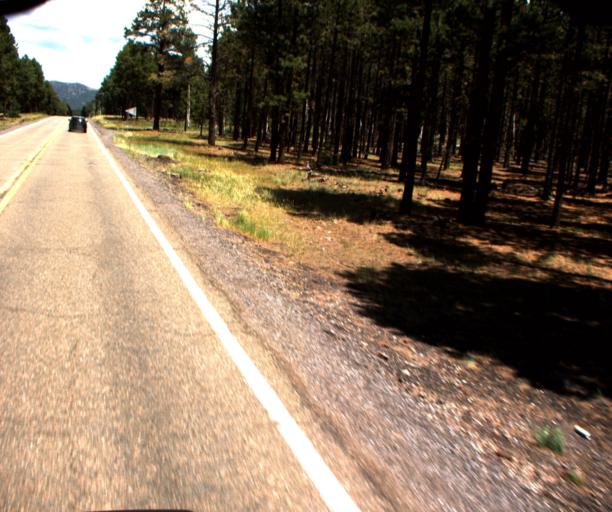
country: US
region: Arizona
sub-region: Coconino County
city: Parks
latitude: 35.3846
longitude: -111.7790
